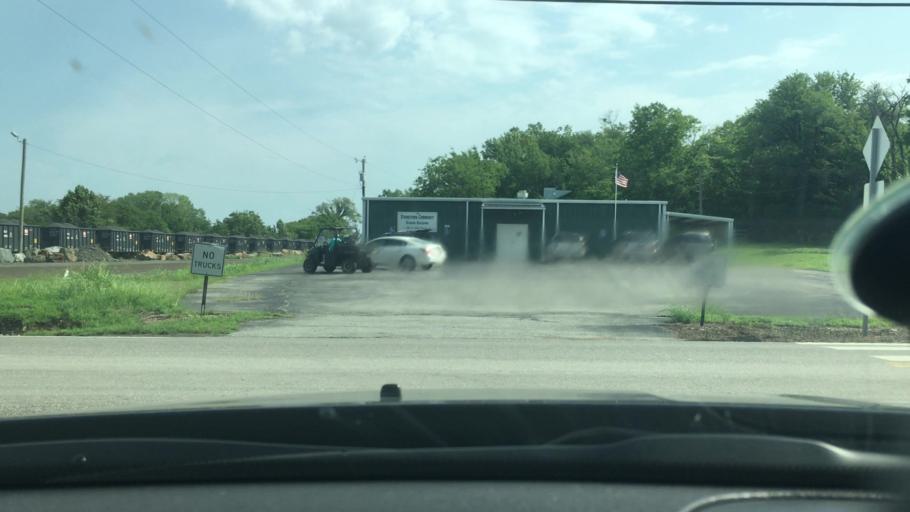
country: US
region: Oklahoma
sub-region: Atoka County
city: Atoka
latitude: 34.4691
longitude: -96.0530
